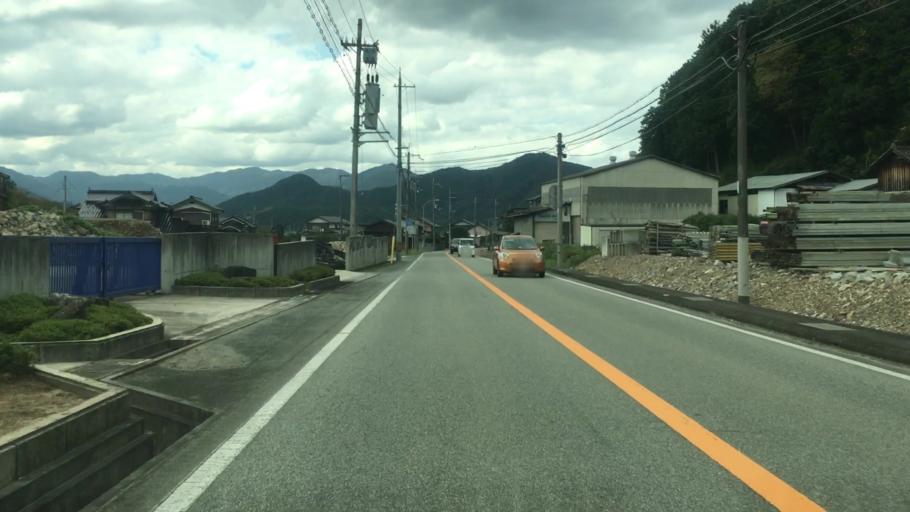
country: JP
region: Kyoto
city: Fukuchiyama
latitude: 35.3083
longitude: 134.9011
